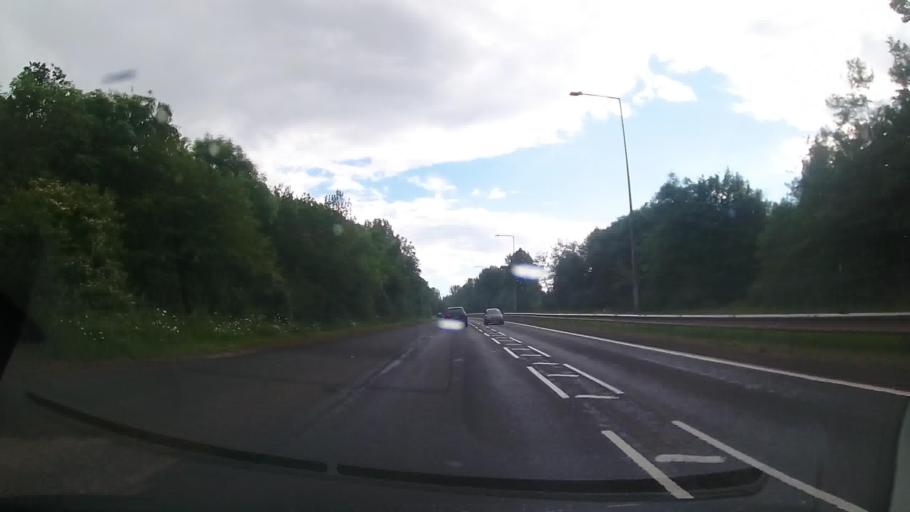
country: GB
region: England
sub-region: Telford and Wrekin
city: Oakengates
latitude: 52.6982
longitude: -2.4647
